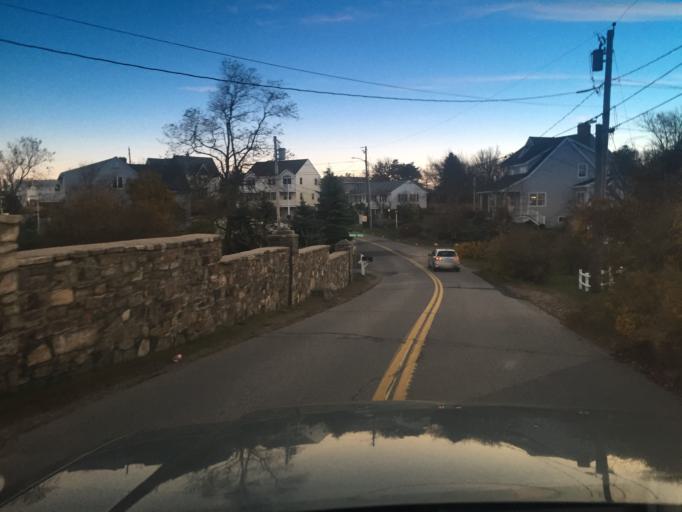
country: US
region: Maine
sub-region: York County
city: York Beach
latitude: 43.1710
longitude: -70.5963
